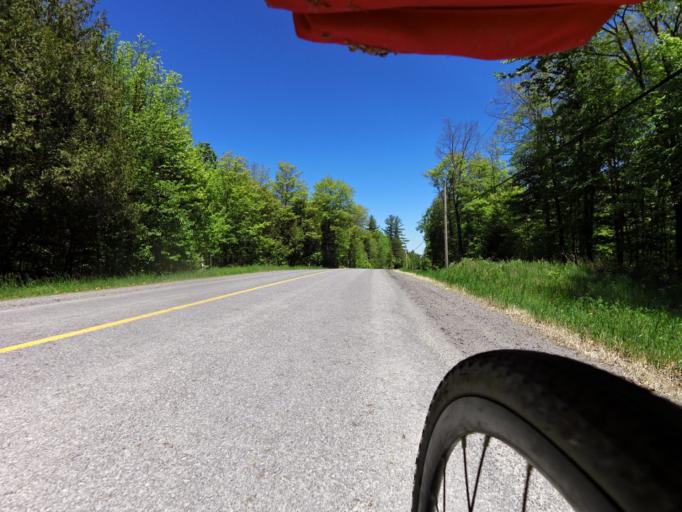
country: CA
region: Ontario
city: Carleton Place
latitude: 45.1680
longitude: -76.4198
